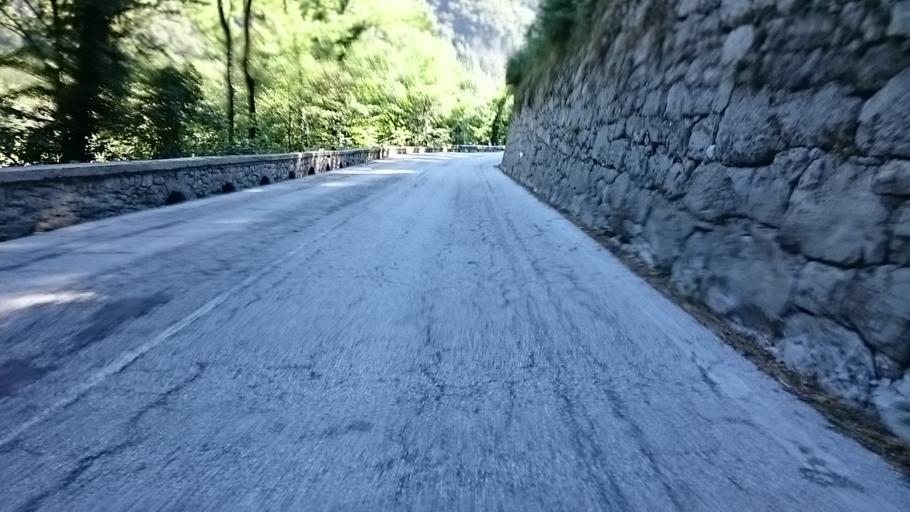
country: IT
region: Veneto
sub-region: Provincia di Belluno
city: Ospitale di Cadore
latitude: 46.3071
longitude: 12.3246
